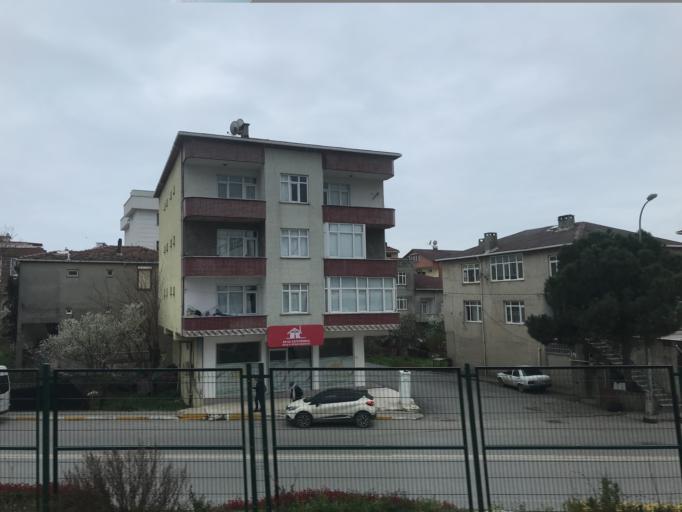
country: TR
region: Istanbul
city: Icmeler
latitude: 40.8379
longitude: 29.3110
